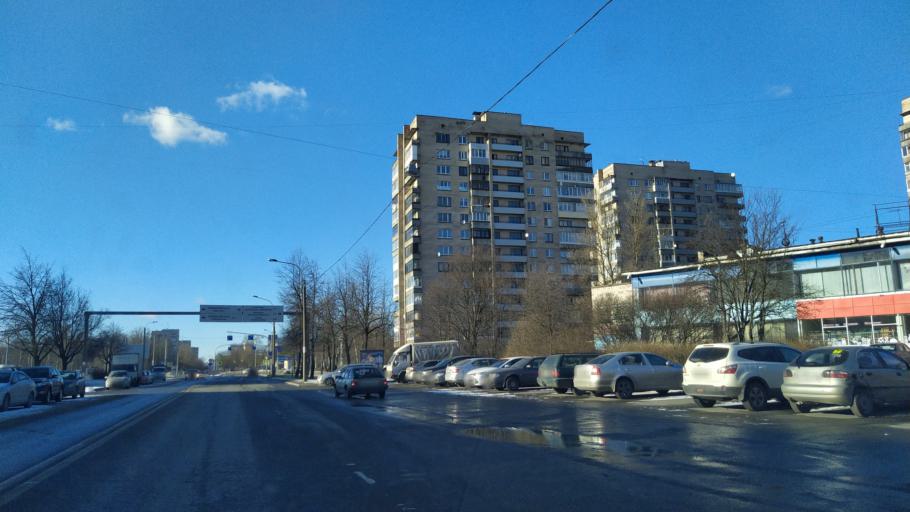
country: RU
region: Leningrad
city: Kalininskiy
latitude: 59.9727
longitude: 30.4174
